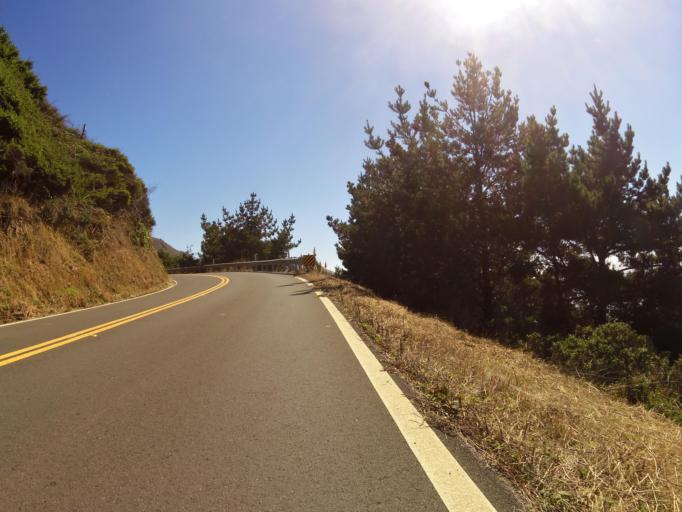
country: US
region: California
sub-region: Mendocino County
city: Fort Bragg
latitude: 39.6256
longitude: -123.7827
